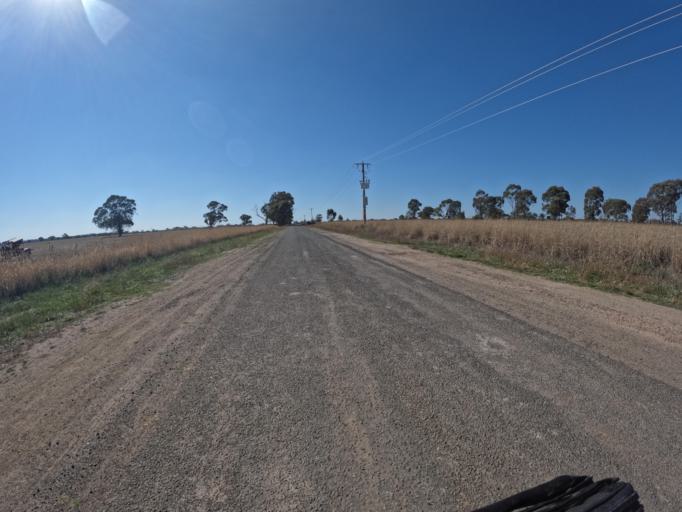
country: AU
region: Victoria
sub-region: Greater Bendigo
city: Epsom
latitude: -36.7891
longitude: 144.5148
